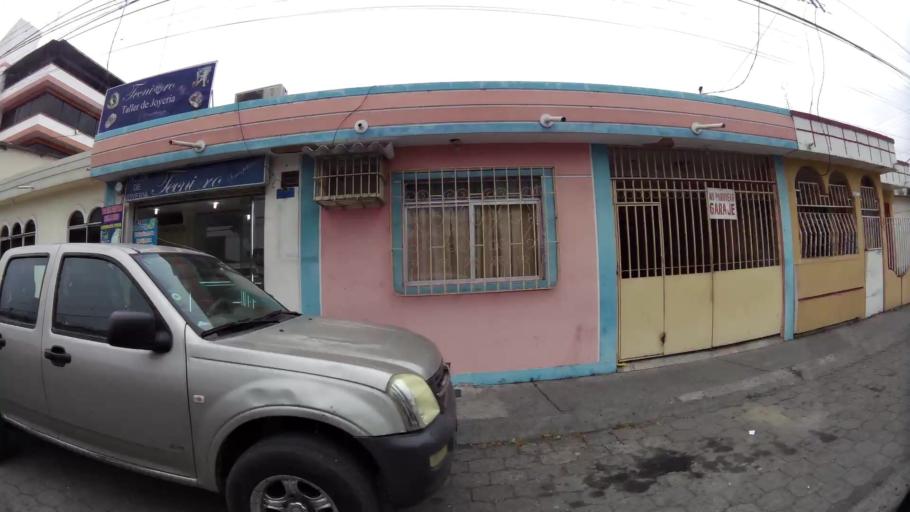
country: EC
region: Guayas
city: Eloy Alfaro
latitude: -2.1369
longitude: -79.8995
